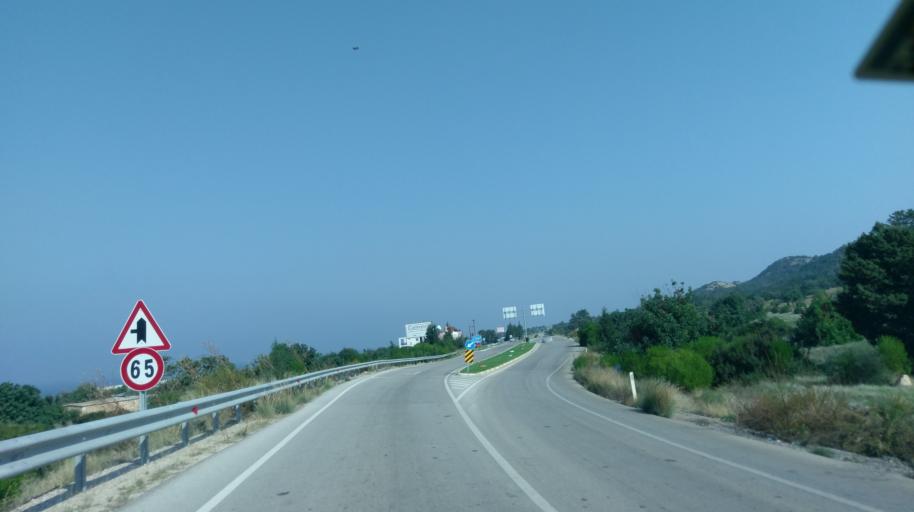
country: CY
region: Ammochostos
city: Lefkonoiko
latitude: 35.3711
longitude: 33.7097
